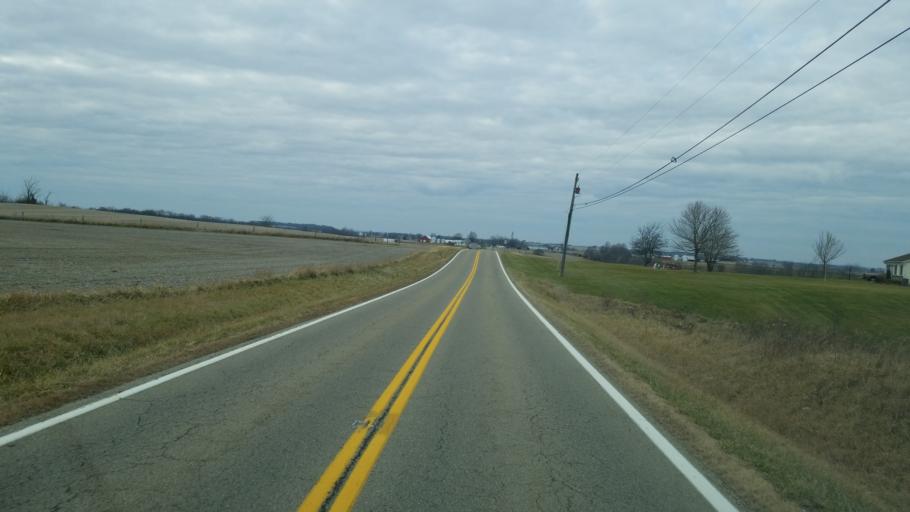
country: US
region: Ohio
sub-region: Highland County
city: Greenfield
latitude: 39.3540
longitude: -83.2881
